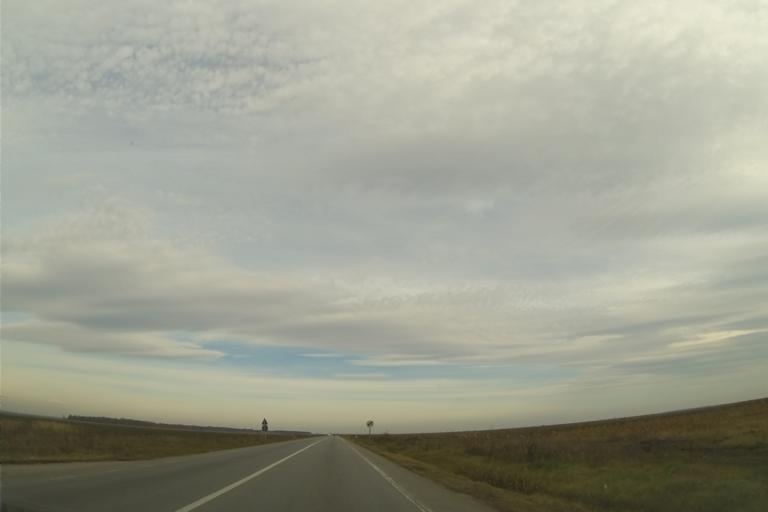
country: RO
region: Olt
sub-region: Comuna Priseaca
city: Priseaca
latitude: 44.4971
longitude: 24.4581
